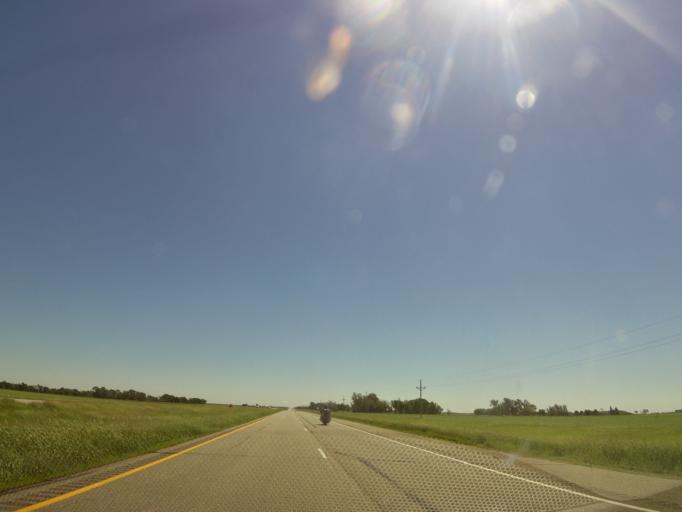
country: US
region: Minnesota
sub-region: Polk County
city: Crookston
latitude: 47.7604
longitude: -96.5325
